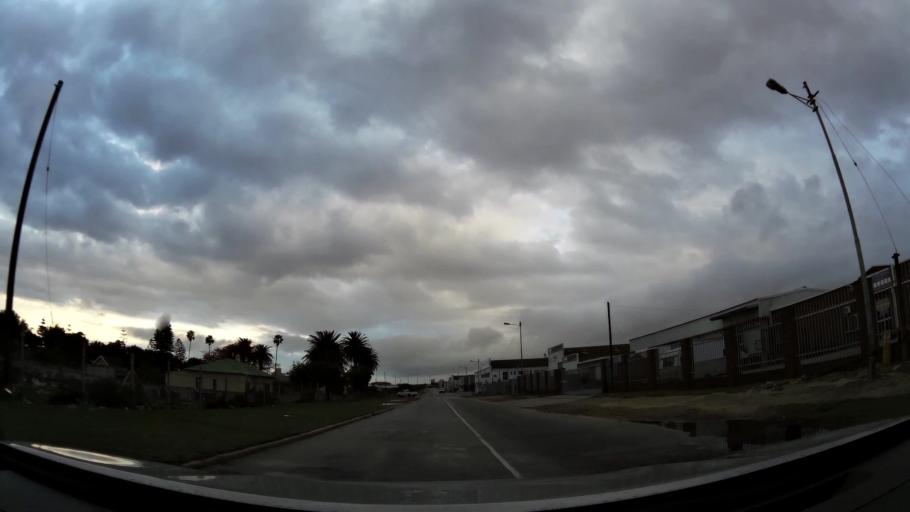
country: ZA
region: Eastern Cape
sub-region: Nelson Mandela Bay Metropolitan Municipality
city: Port Elizabeth
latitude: -33.9239
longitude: 25.6061
